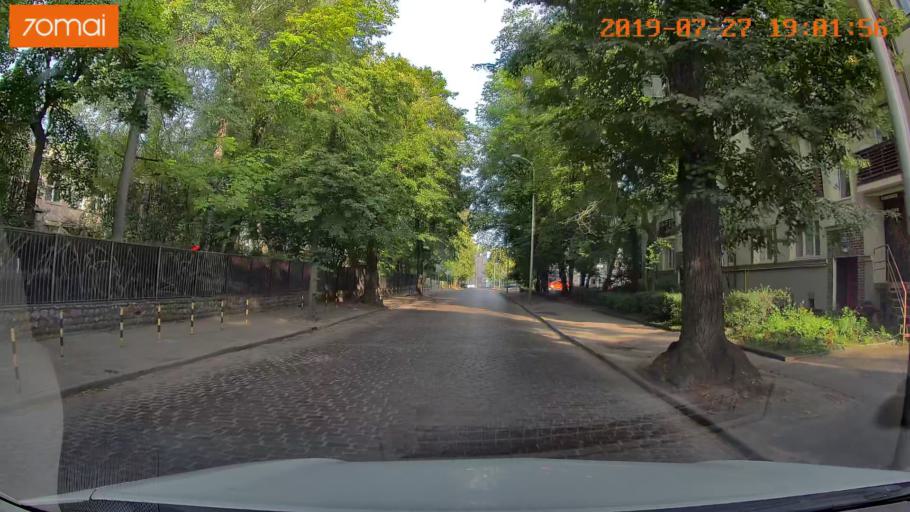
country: RU
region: Kaliningrad
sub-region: Gorod Kaliningrad
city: Kaliningrad
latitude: 54.7256
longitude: 20.4912
